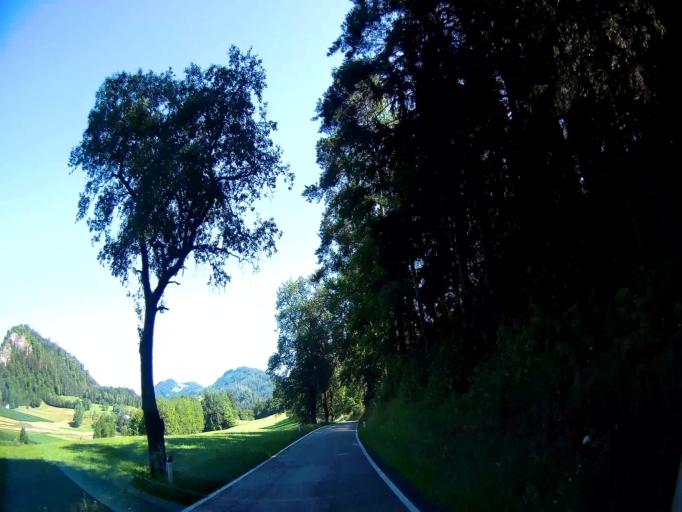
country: AT
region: Carinthia
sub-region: Politischer Bezirk Volkermarkt
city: Voelkermarkt
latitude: 46.6884
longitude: 14.5775
